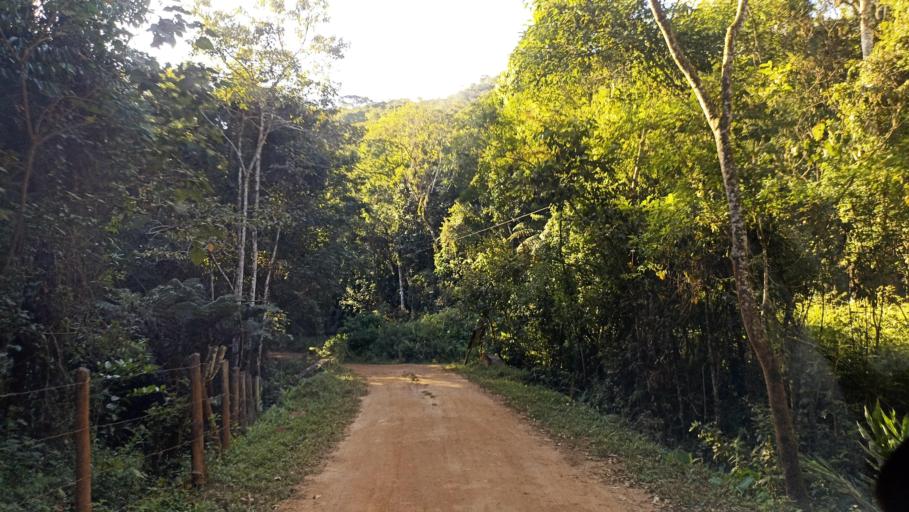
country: BR
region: Minas Gerais
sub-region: Ouro Preto
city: Ouro Preto
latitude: -20.2933
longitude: -43.5710
